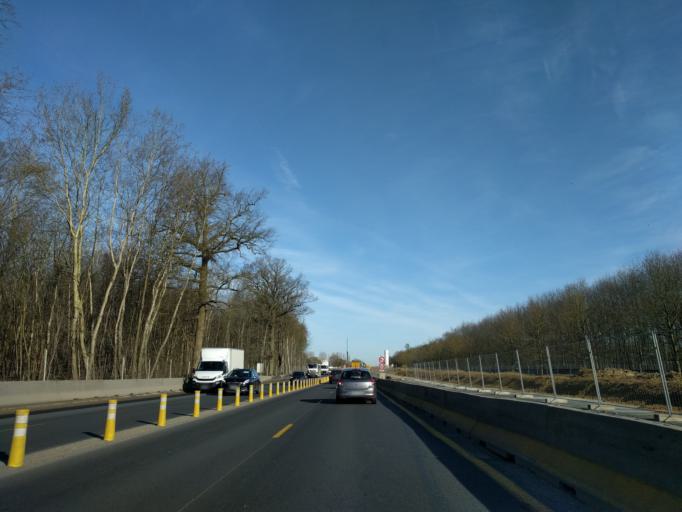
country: FR
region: Ile-de-France
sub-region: Departement du Val-de-Marne
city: Boissy-Saint-Leger
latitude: 48.7386
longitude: 2.5167
